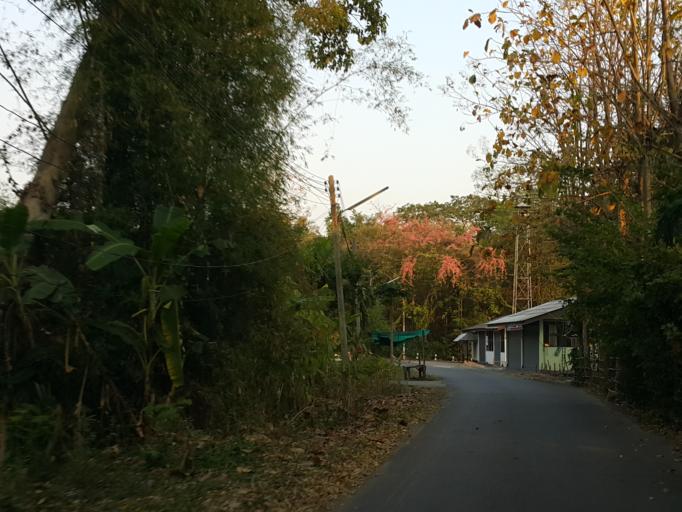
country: TH
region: Chiang Mai
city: San Sai
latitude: 18.8967
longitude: 98.9536
